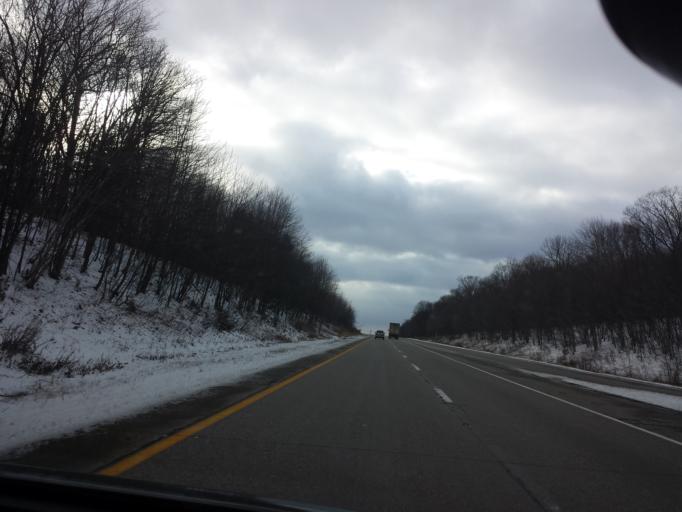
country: US
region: Pennsylvania
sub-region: Luzerne County
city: Conyngham
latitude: 41.0459
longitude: -76.0163
